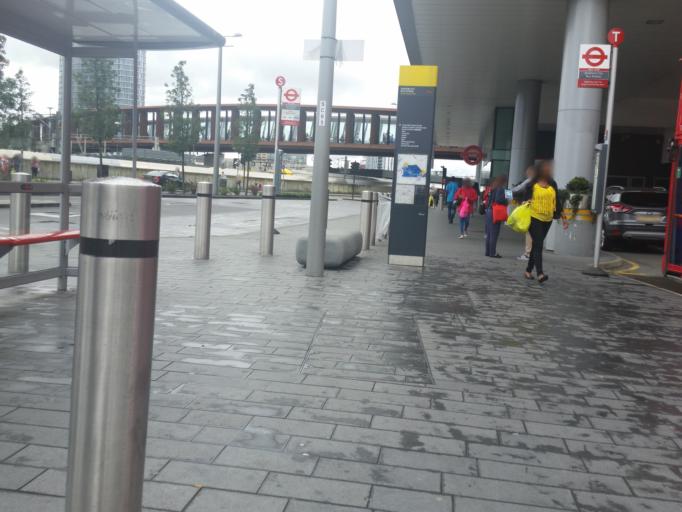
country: GB
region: England
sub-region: Greater London
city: Poplar
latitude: 51.5433
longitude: -0.0043
